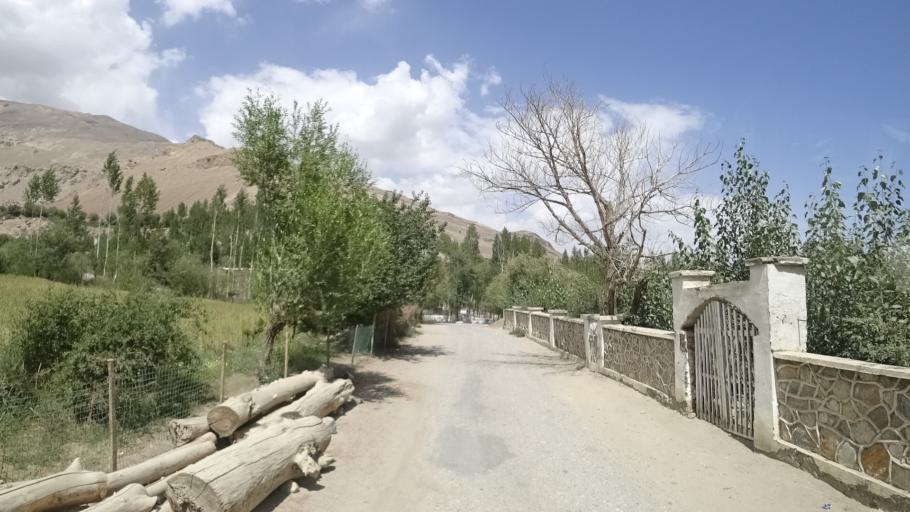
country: AF
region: Badakhshan
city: Khandud
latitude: 36.9460
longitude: 72.2296
